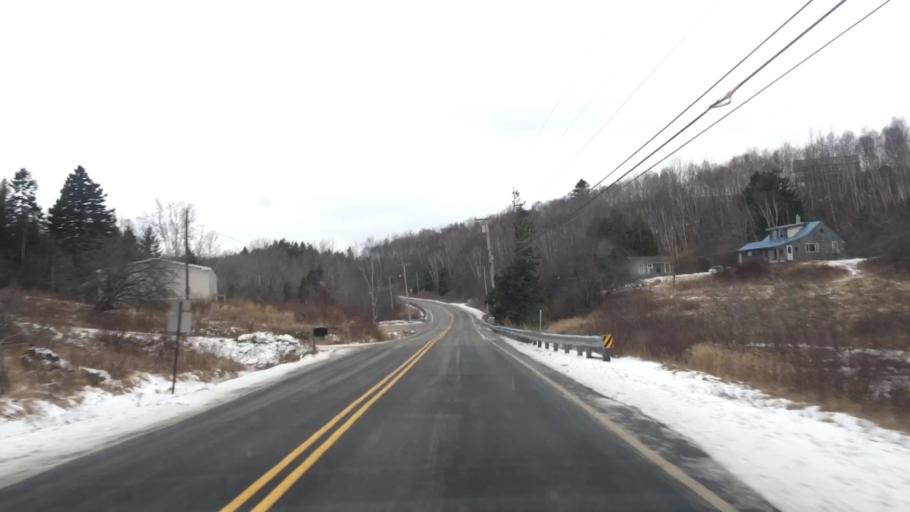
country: US
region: Maine
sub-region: Washington County
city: Machiasport
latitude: 44.7125
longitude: -67.3737
